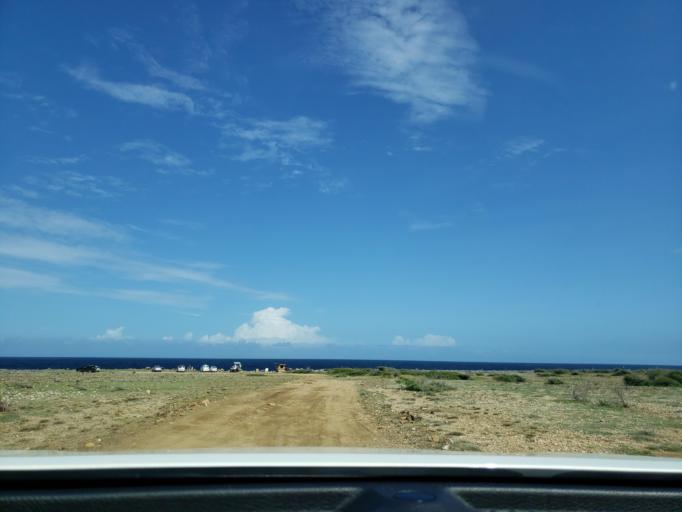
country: CW
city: Barber
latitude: 12.3641
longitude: -69.1100
